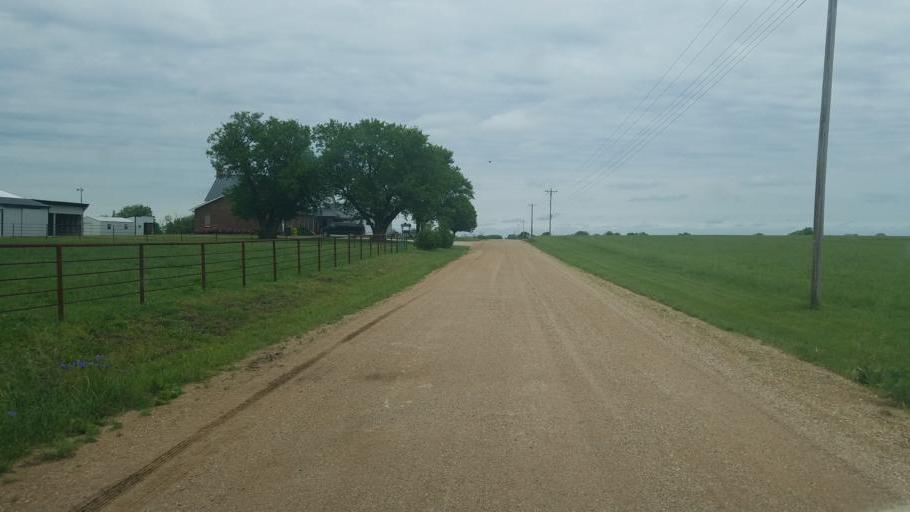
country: US
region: Missouri
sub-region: Morgan County
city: Versailles
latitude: 38.4946
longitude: -92.7900
